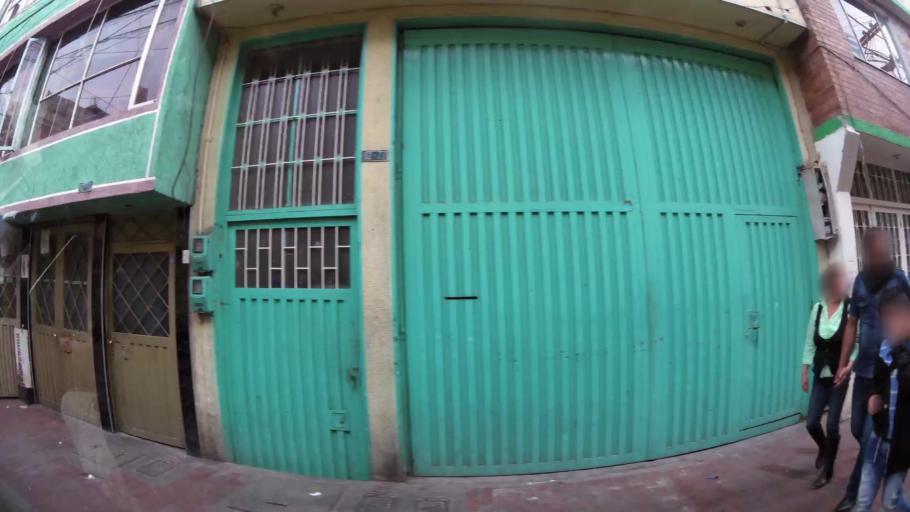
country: CO
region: Bogota D.C.
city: Bogota
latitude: 4.6378
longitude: -74.1574
